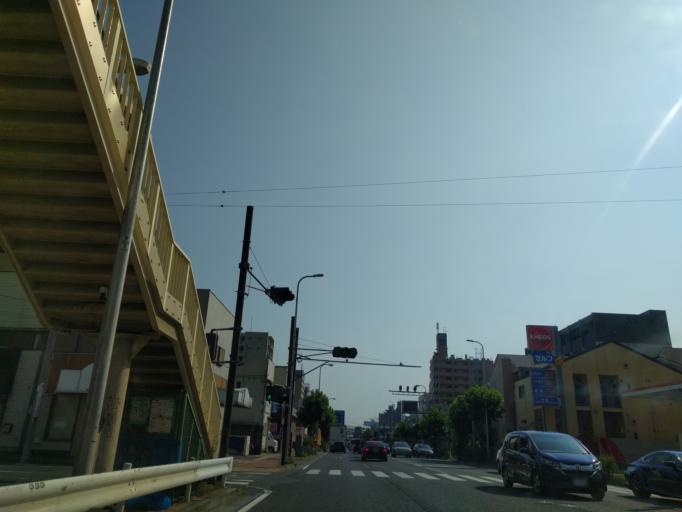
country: JP
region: Kanagawa
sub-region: Kawasaki-shi
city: Kawasaki
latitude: 35.4961
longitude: 139.6700
